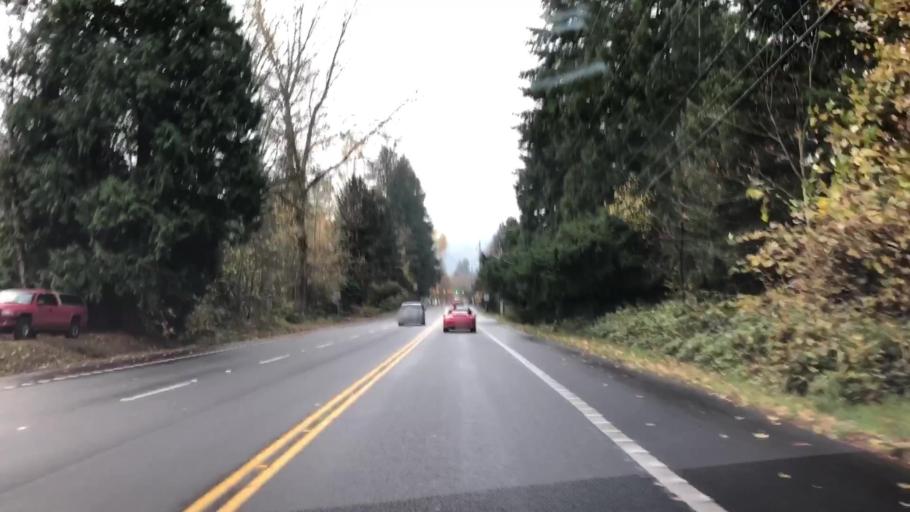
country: US
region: Washington
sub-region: King County
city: Woodinville
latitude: 47.7587
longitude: -122.1477
